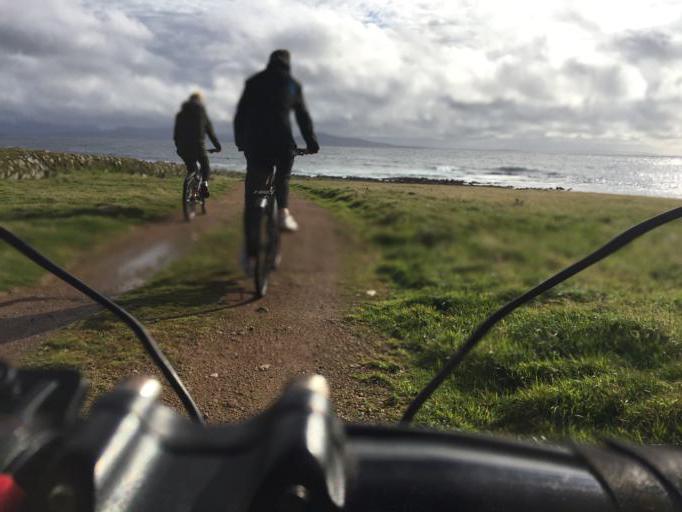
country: IE
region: Ulster
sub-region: County Donegal
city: Derrybeg
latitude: 55.2634
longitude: -8.2342
